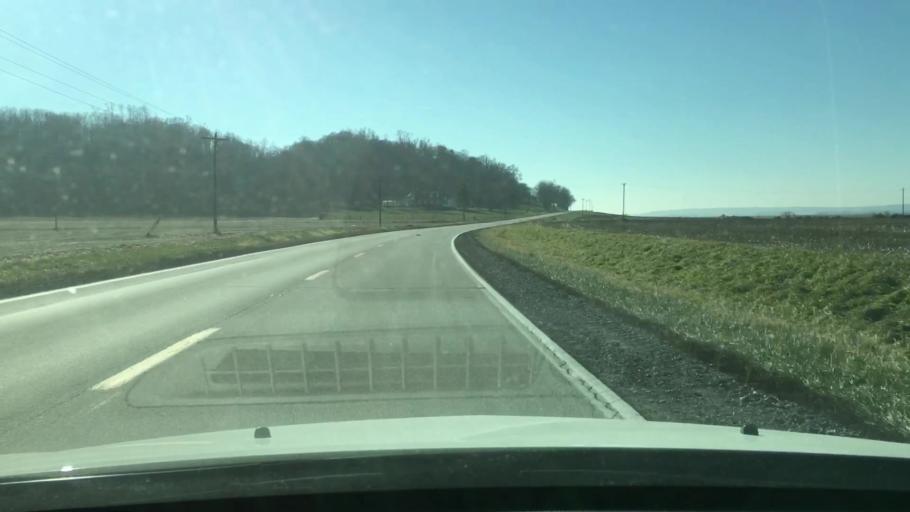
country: US
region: Illinois
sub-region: Morgan County
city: Meredosia
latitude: 39.7049
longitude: -90.5690
